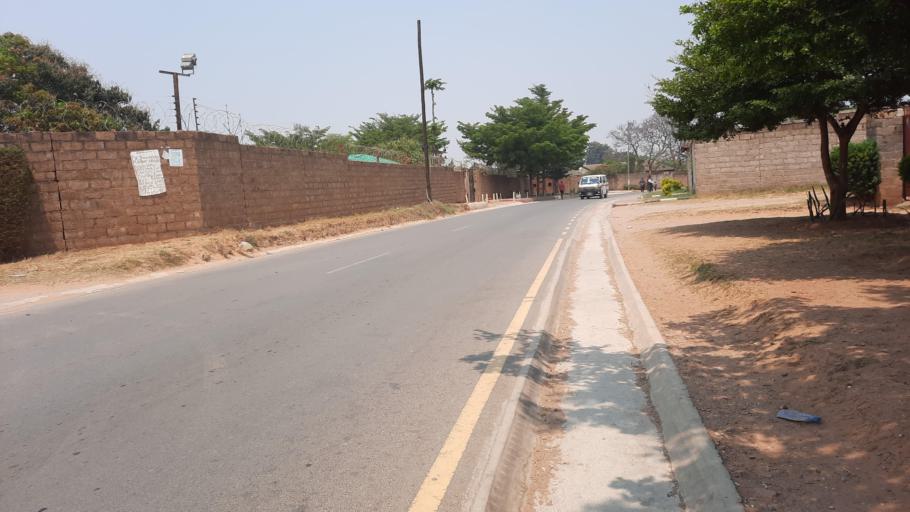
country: ZM
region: Lusaka
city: Lusaka
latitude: -15.4112
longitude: 28.3656
